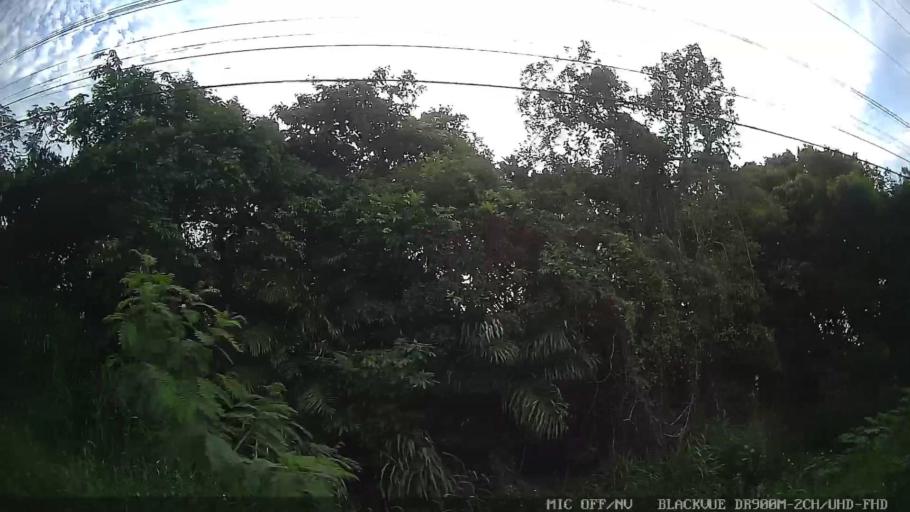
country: BR
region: Sao Paulo
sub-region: Itanhaem
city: Itanhaem
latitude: -24.1595
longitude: -46.7819
